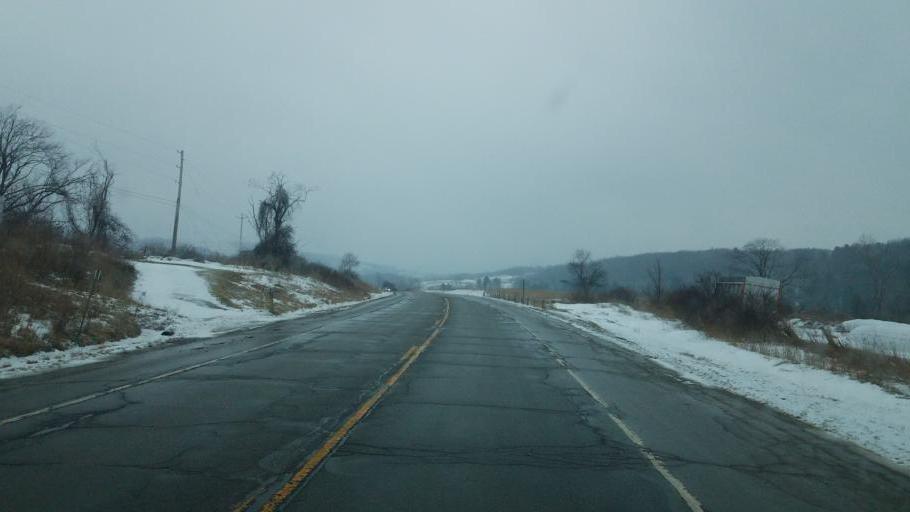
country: US
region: Pennsylvania
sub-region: Tioga County
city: Elkland
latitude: 42.0984
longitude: -77.4440
